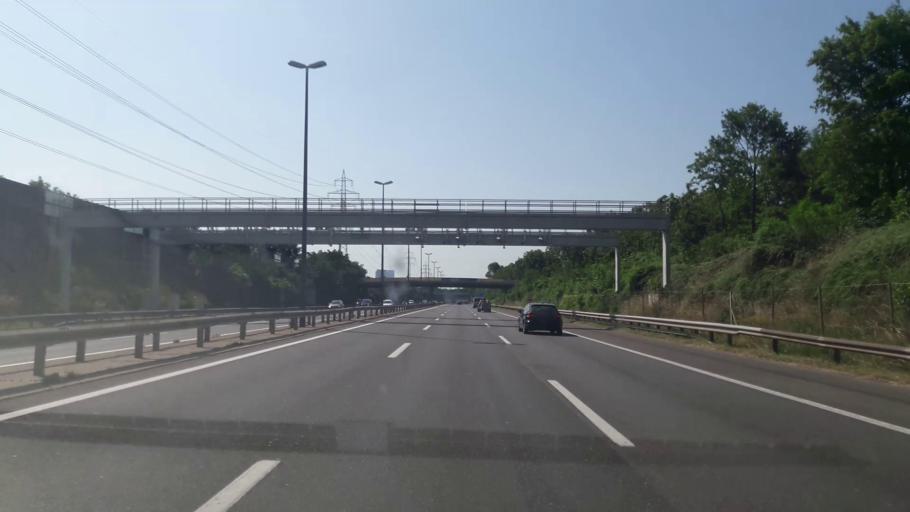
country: AT
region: Lower Austria
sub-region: Politischer Bezirk Korneuburg
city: Langenzersdorf
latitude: 48.2742
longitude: 16.3709
